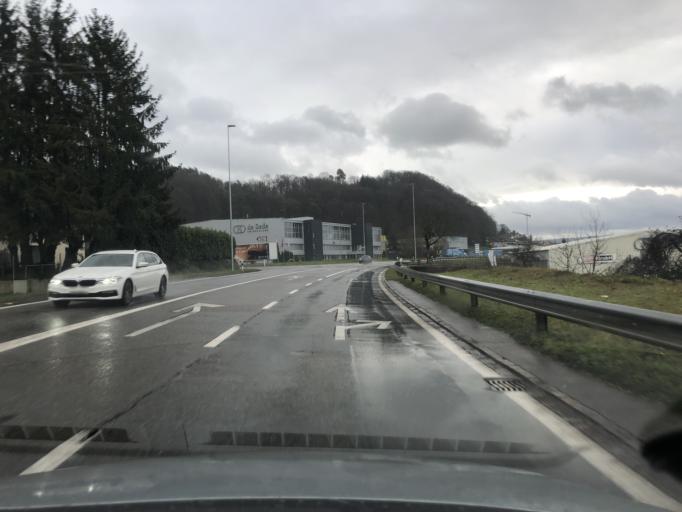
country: CH
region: Aargau
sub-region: Bezirk Zurzach
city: Koblenz
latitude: 47.5931
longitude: 8.2383
